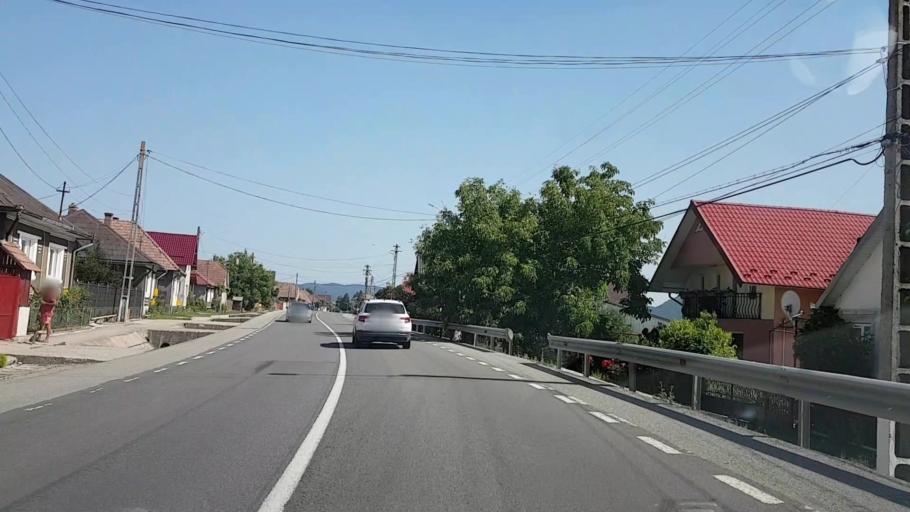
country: RO
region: Bistrita-Nasaud
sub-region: Comuna Sieu-Magherus
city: Sieu-Magherus
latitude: 47.0944
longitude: 24.3690
